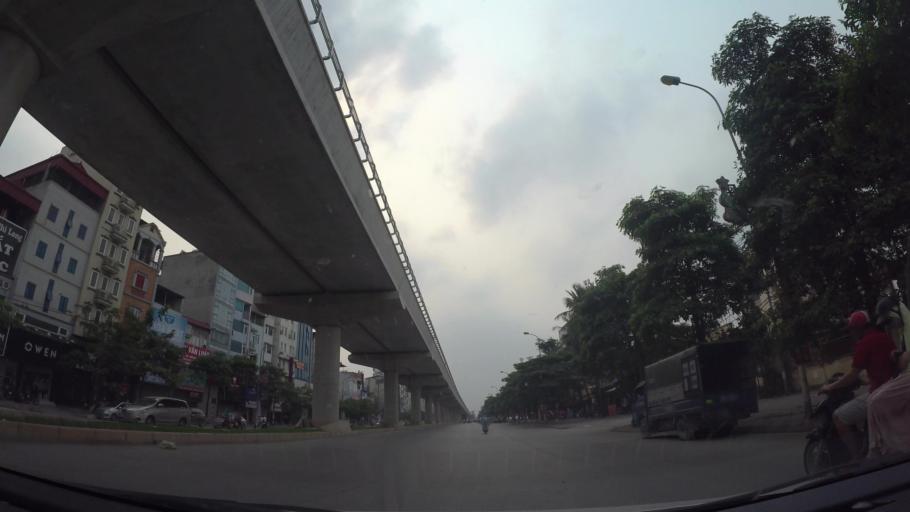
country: VN
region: Ha Noi
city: Cau Dien
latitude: 21.0450
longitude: 105.7528
